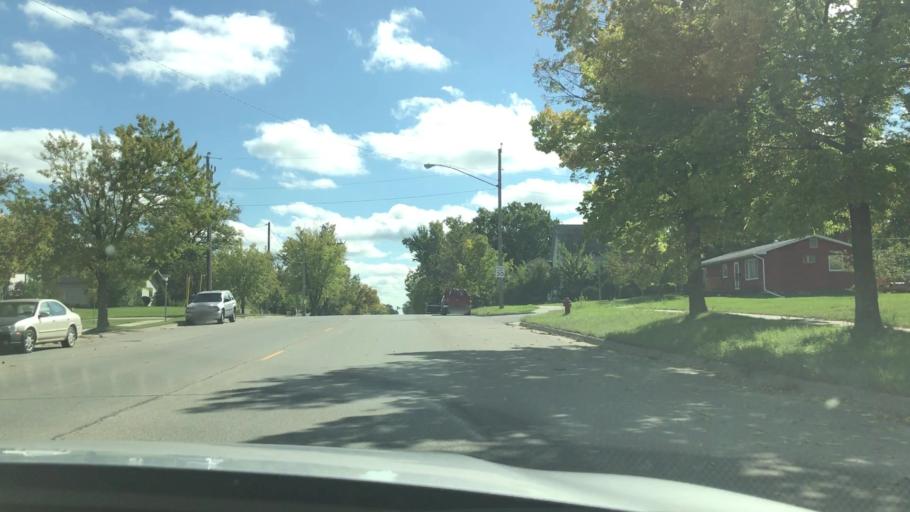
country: US
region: Minnesota
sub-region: Hubbard County
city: Park Rapids
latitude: 46.9261
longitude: -95.0585
